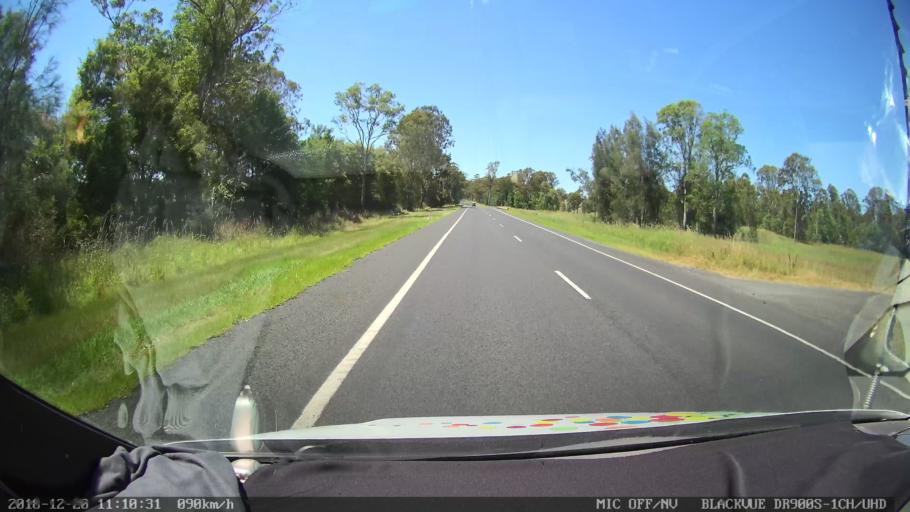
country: AU
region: New South Wales
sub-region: Richmond Valley
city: Casino
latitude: -28.9502
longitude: 153.0094
